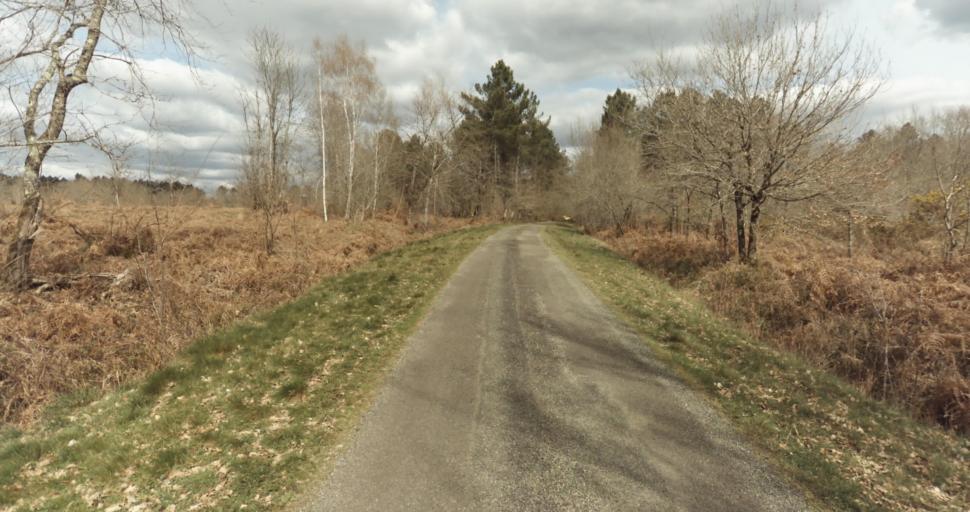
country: FR
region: Aquitaine
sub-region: Departement des Landes
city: Roquefort
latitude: 44.0781
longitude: -0.3959
